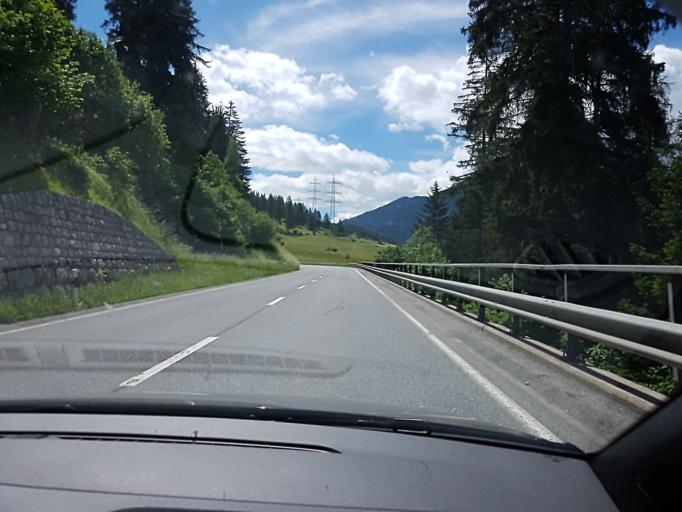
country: CH
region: Grisons
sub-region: Albula District
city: Tiefencastel
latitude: 46.6174
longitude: 9.5923
